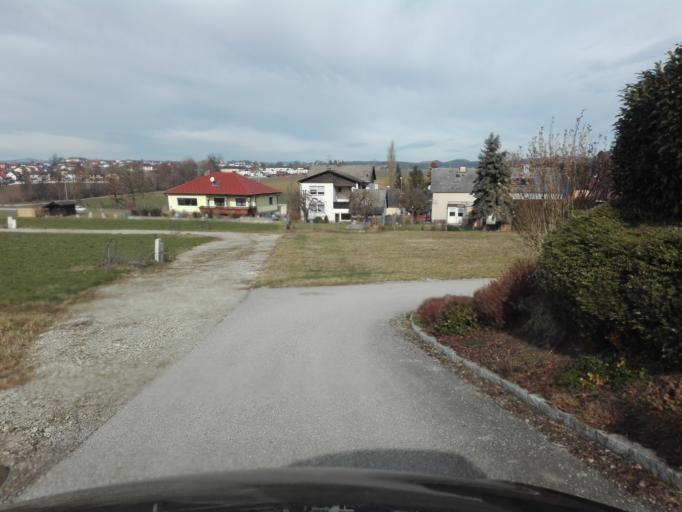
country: AT
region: Lower Austria
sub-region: Politischer Bezirk Amstetten
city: Ennsdorf
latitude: 48.2693
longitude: 14.5369
